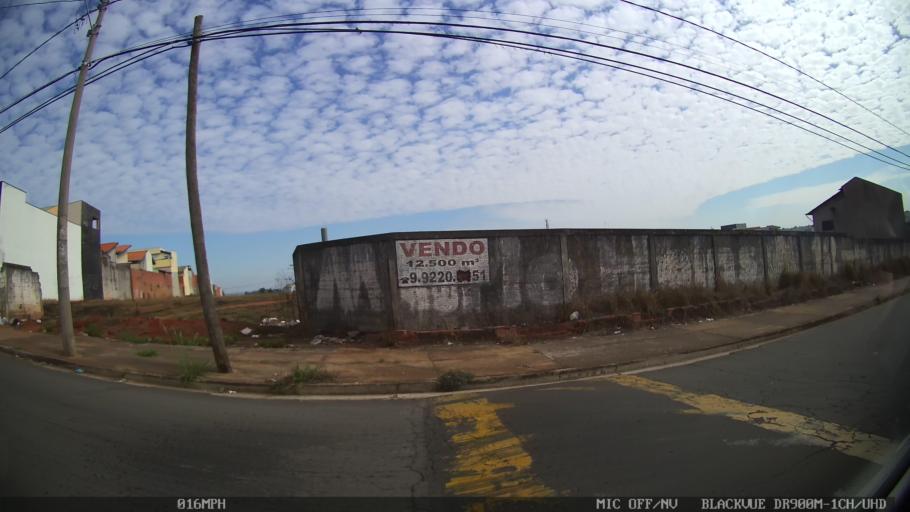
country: BR
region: Sao Paulo
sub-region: Santa Barbara D'Oeste
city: Santa Barbara d'Oeste
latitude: -22.7676
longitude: -47.3998
